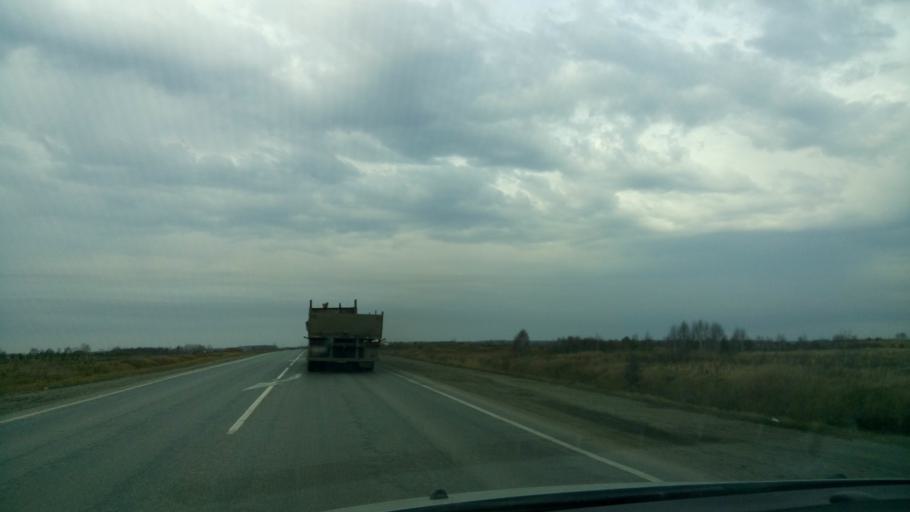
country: RU
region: Sverdlovsk
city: Kamyshlov
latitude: 56.8727
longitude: 62.7356
